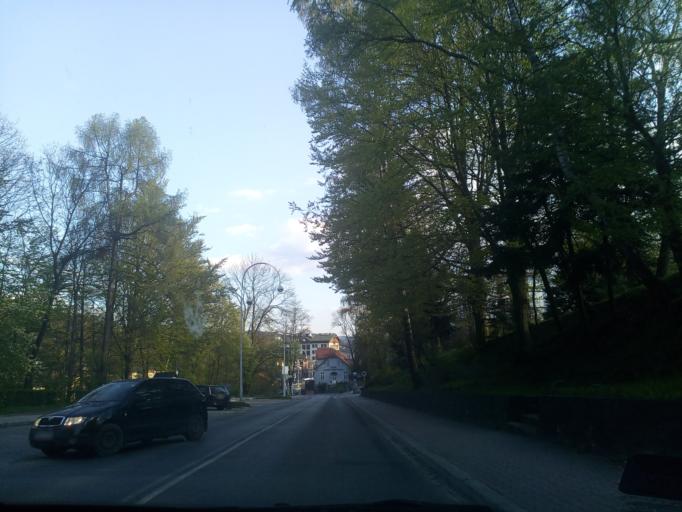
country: PL
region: Lesser Poland Voivodeship
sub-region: Powiat nowosadecki
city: Krynica-Zdroj
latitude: 49.4167
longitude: 20.9550
